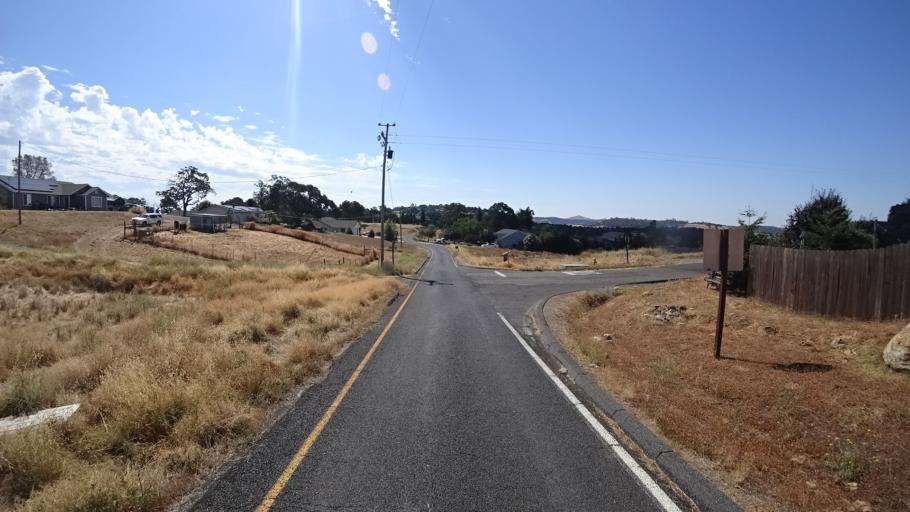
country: US
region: California
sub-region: Calaveras County
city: Copperopolis
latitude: 37.9189
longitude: -120.6219
